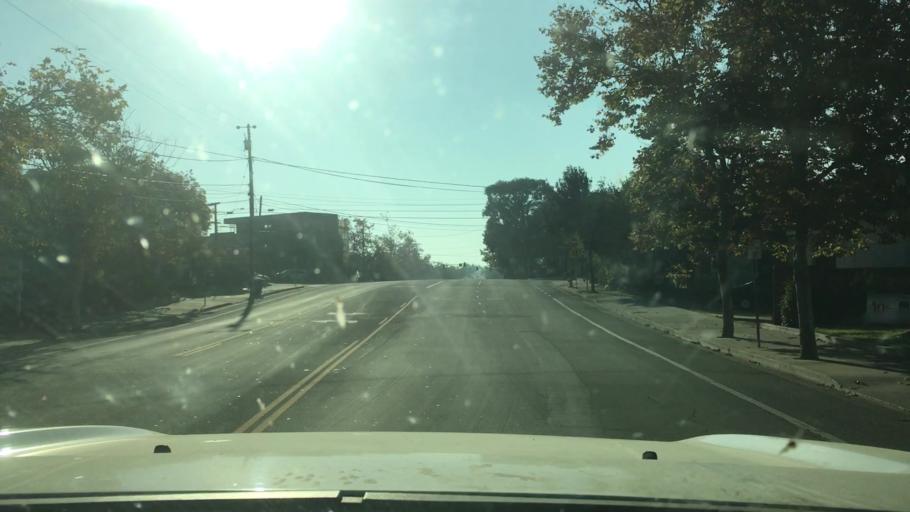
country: US
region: California
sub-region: San Luis Obispo County
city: San Luis Obispo
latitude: 35.2719
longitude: -120.6583
